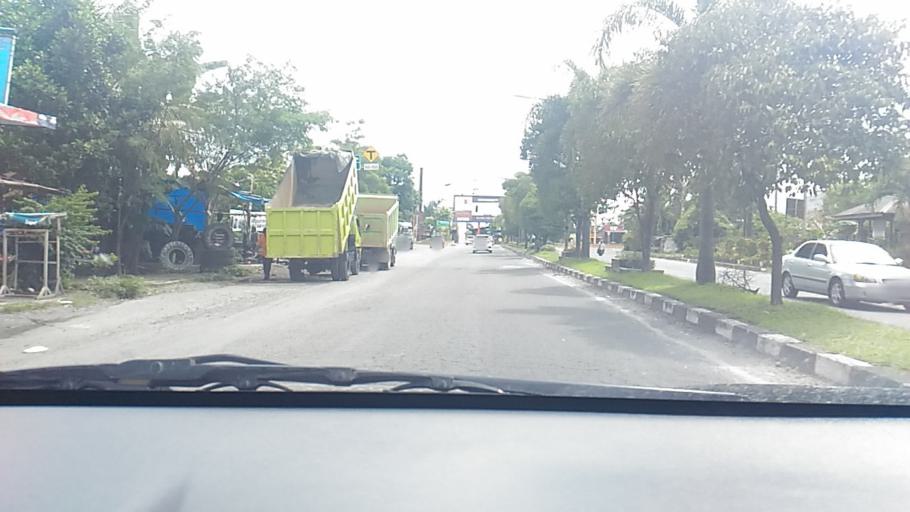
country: ID
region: North Sumatra
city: Binjai
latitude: 3.6504
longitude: 98.5123
